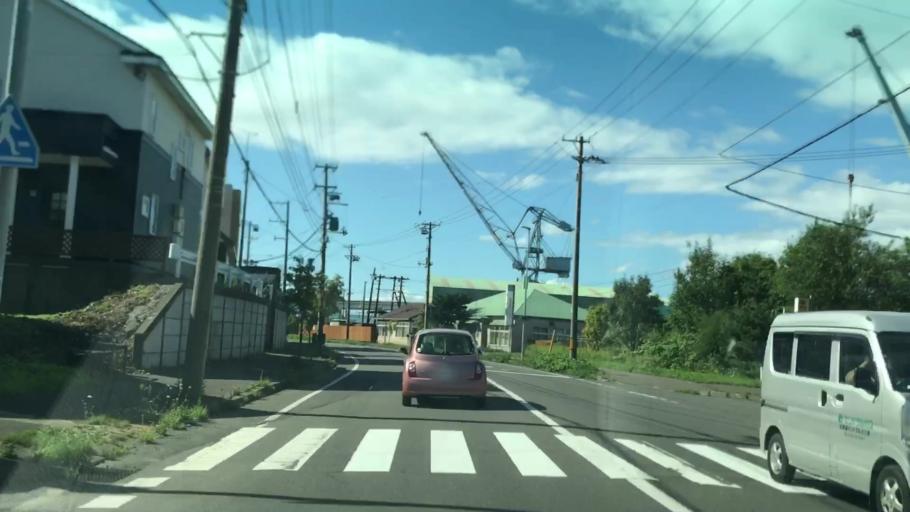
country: JP
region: Hokkaido
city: Muroran
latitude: 42.3378
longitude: 140.9556
